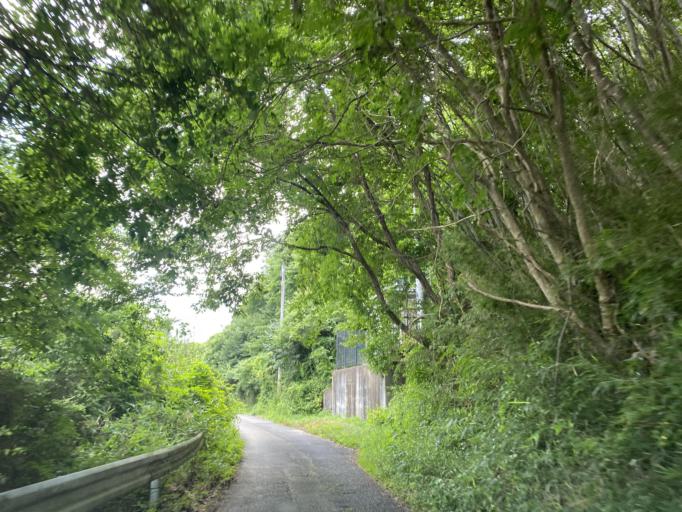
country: JP
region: Fukushima
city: Koriyama
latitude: 37.3753
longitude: 140.4222
